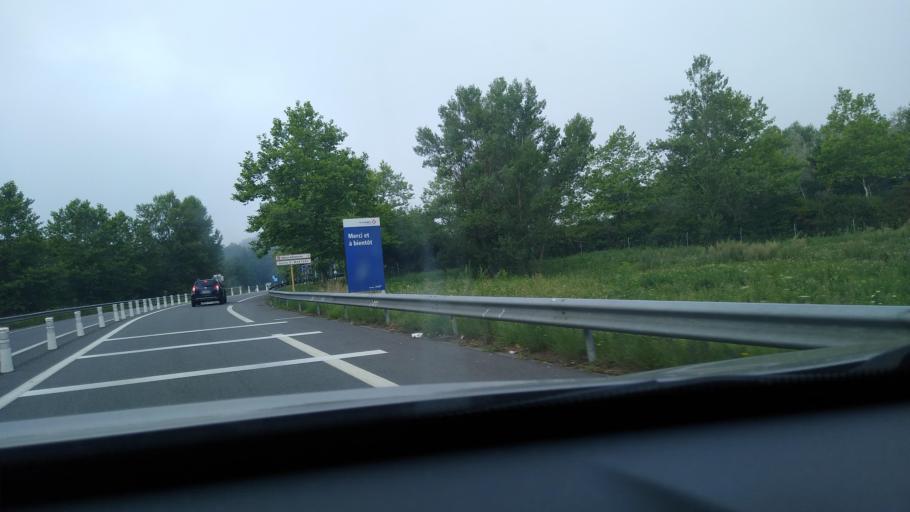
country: FR
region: Midi-Pyrenees
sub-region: Departement de la Haute-Garonne
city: Salies-du-Salat
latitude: 43.1238
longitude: 0.9368
